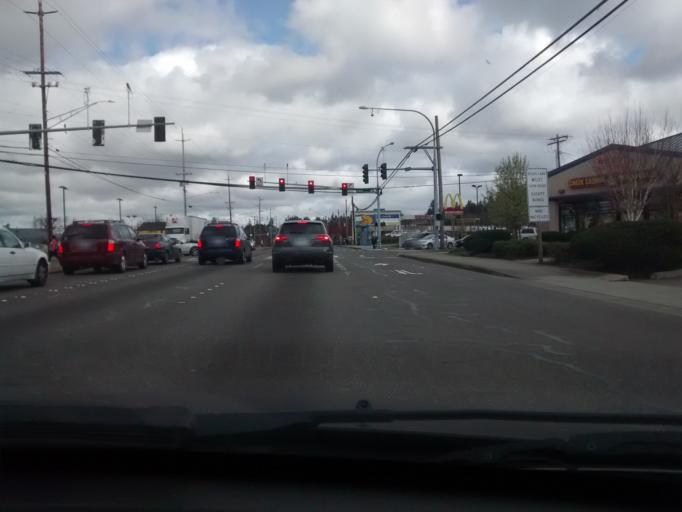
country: US
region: Washington
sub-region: Snohomish County
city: Lynnwood
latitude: 47.8387
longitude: -122.2998
